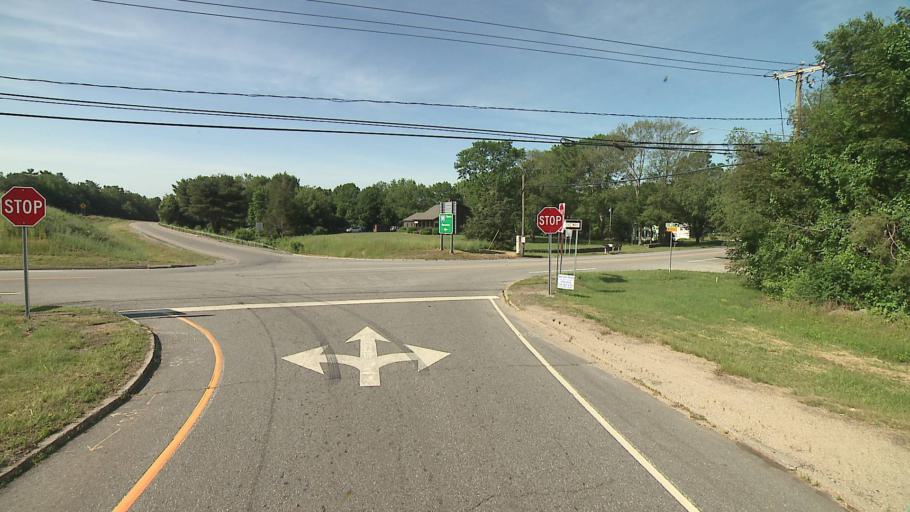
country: US
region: Connecticut
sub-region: New London County
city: Jewett City
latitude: 41.6144
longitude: -71.9468
